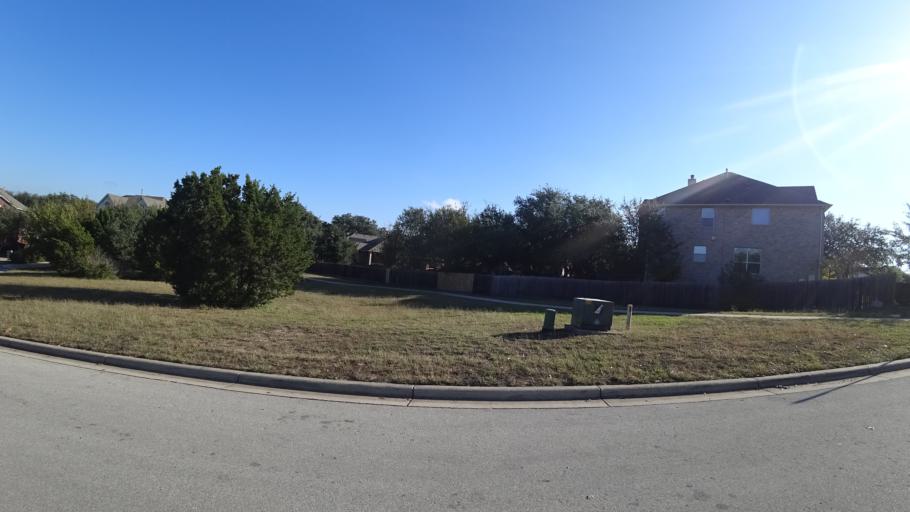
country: US
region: Texas
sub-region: Travis County
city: Hudson Bend
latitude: 30.3675
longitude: -97.8982
